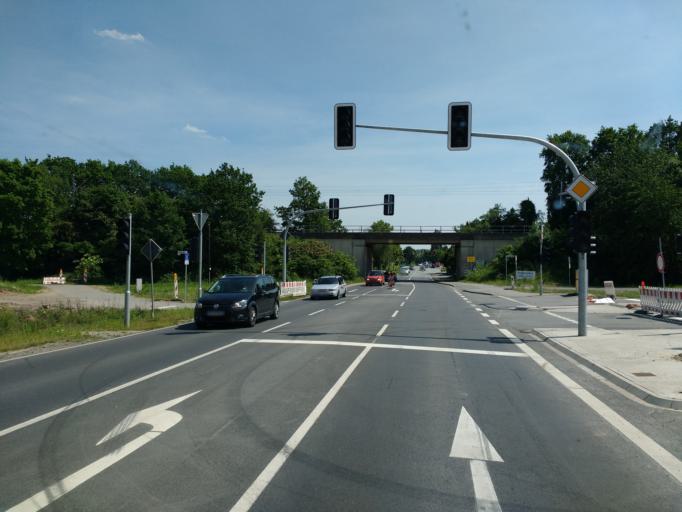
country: DE
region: Lower Saxony
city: Belm
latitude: 52.3072
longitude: 8.1206
